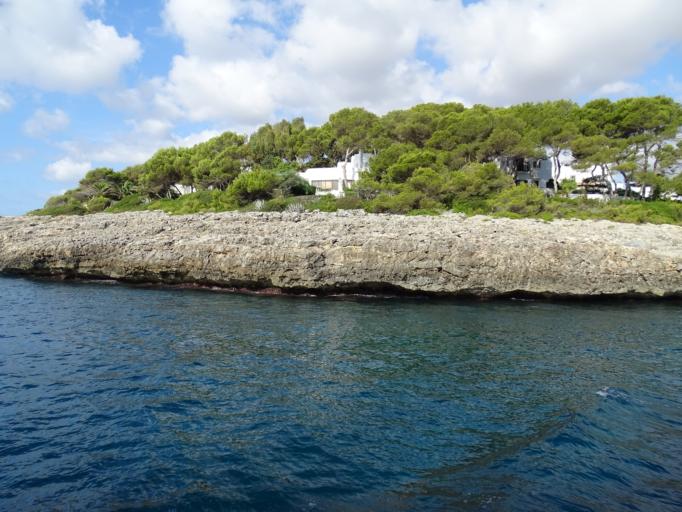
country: ES
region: Balearic Islands
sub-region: Illes Balears
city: Santanyi
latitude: 39.3706
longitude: 3.2345
